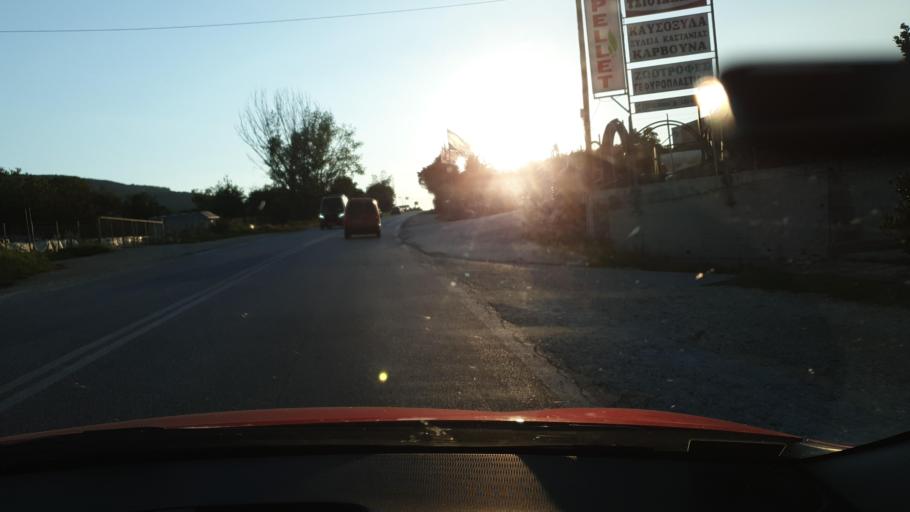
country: GR
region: Central Macedonia
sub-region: Nomos Thessalonikis
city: Nea Apollonia
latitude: 40.5035
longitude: 23.4567
